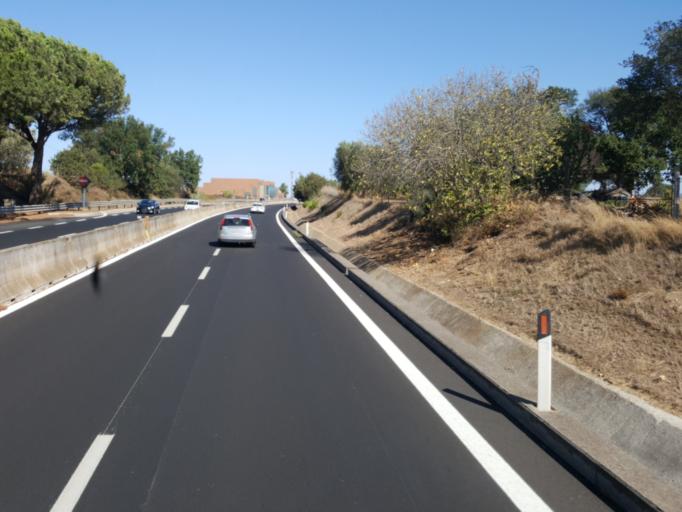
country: IT
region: Latium
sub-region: Provincia di Viterbo
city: Montalto di Castro
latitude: 42.3378
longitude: 11.6205
